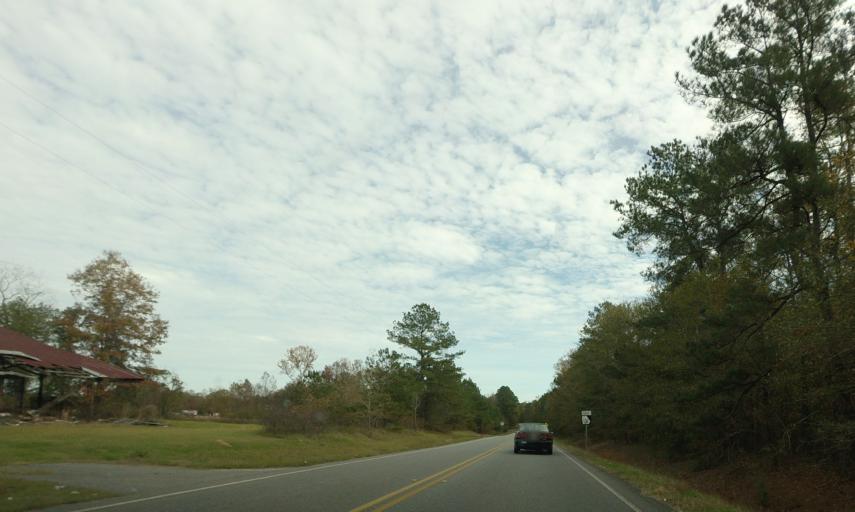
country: US
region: Georgia
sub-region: Dodge County
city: Chester
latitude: 32.4091
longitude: -83.2216
